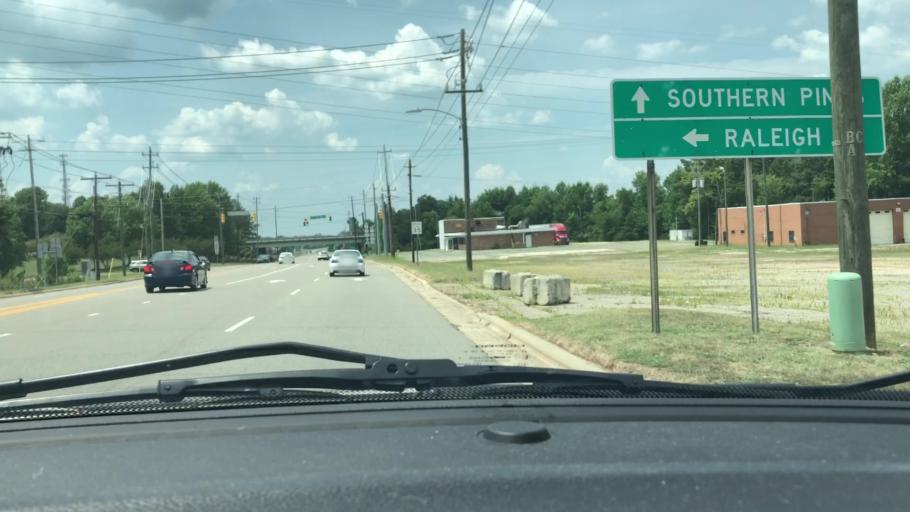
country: US
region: North Carolina
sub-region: Lee County
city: Sanford
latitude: 35.4936
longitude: -79.1929
